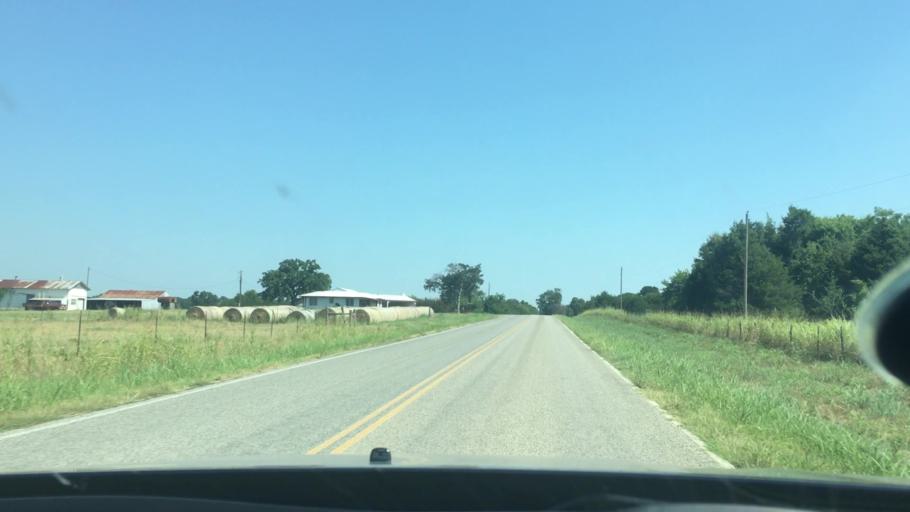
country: US
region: Oklahoma
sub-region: Johnston County
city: Tishomingo
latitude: 34.2773
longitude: -96.6186
